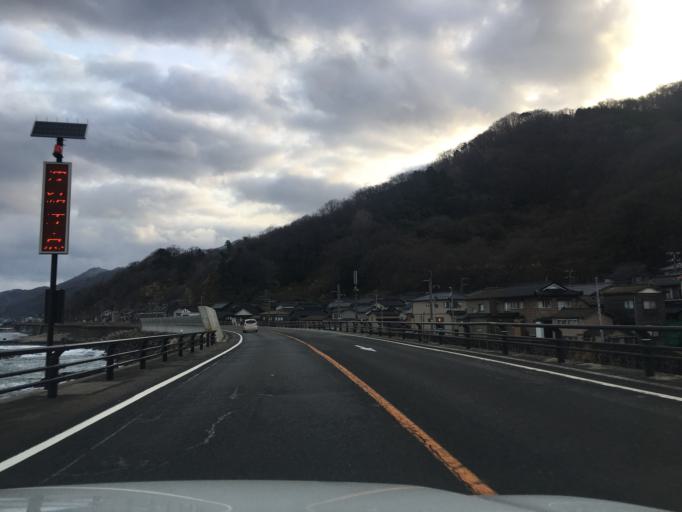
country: JP
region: Yamagata
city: Tsuruoka
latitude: 38.6108
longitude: 139.5759
